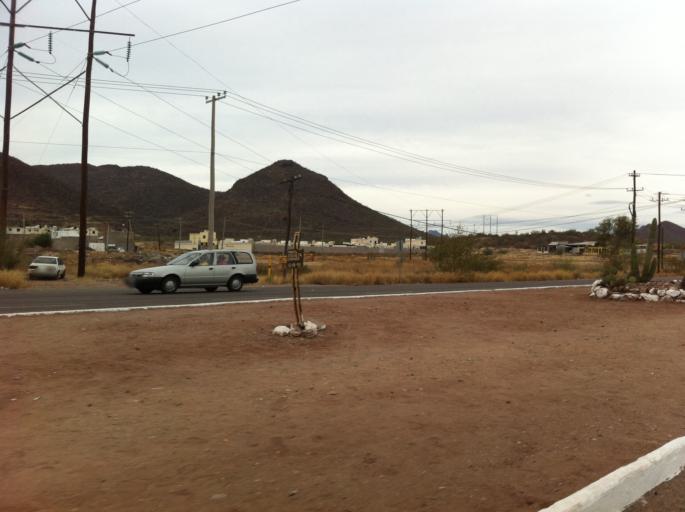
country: MX
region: Sonora
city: Heroica Guaymas
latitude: 27.9466
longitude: -110.9333
